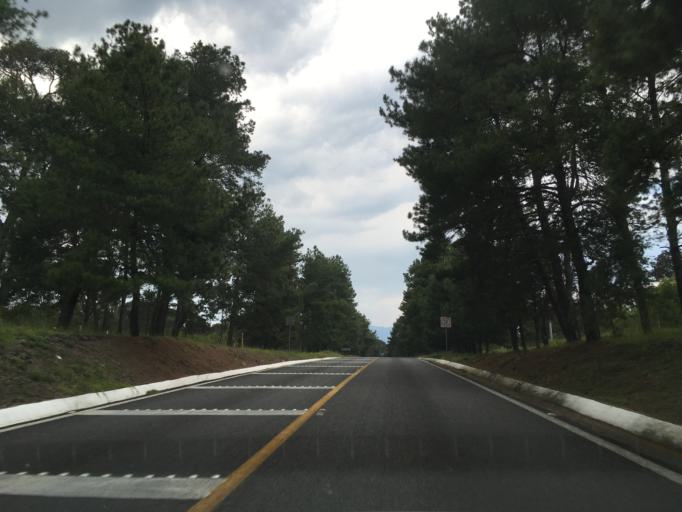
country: MX
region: Michoacan
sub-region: Patzcuaro
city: Santa Maria Huiramangaro (San Juan Tumbio)
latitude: 19.4895
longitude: -101.7200
